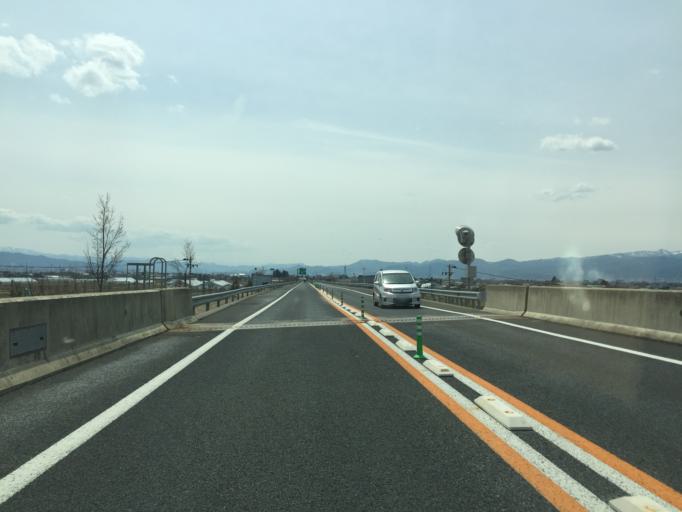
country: JP
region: Yamagata
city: Tendo
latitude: 38.3267
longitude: 140.3275
